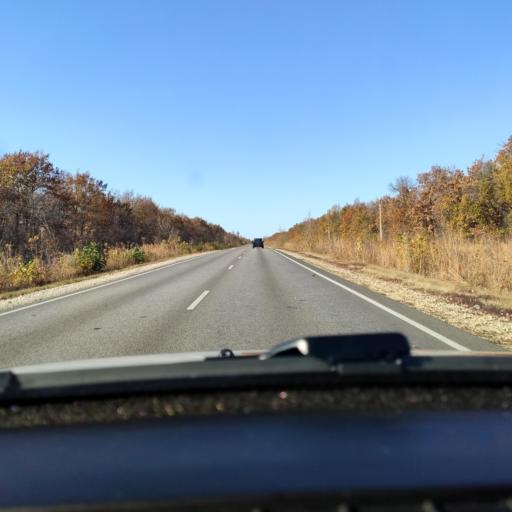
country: RU
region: Voronezj
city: Zemlyansk
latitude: 51.8297
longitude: 38.8275
